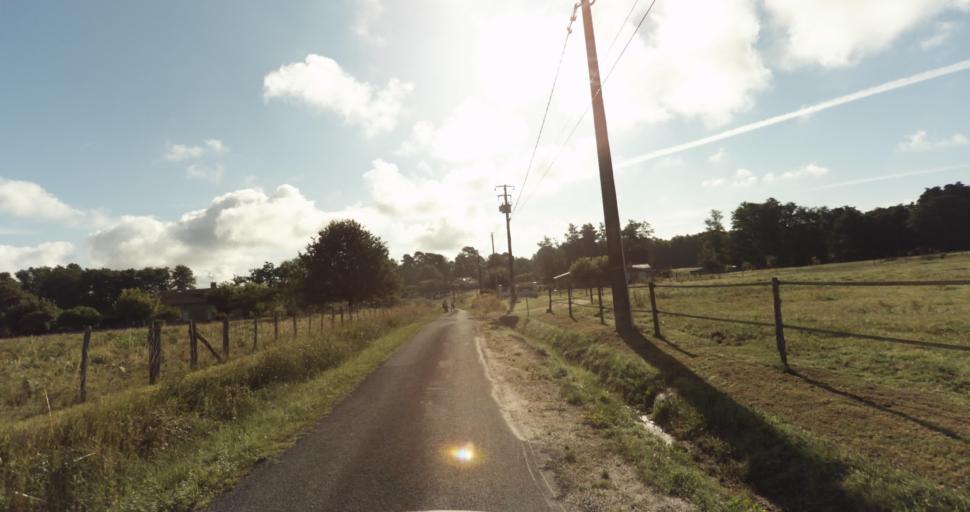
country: FR
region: Aquitaine
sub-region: Departement de la Gironde
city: Bazas
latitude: 44.4467
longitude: -0.2591
